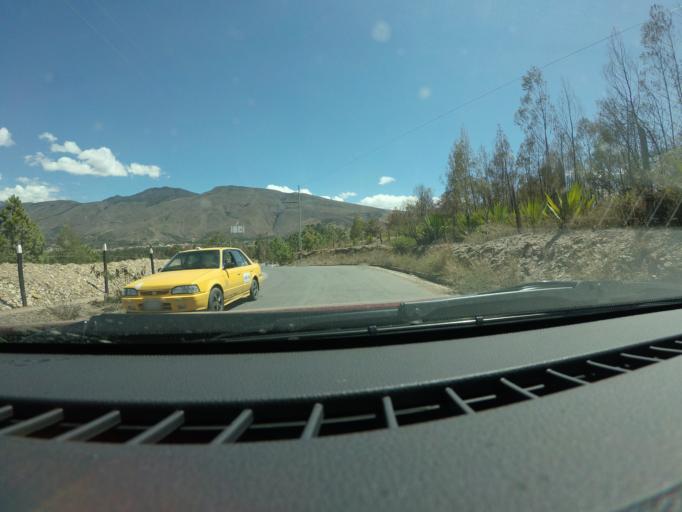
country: CO
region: Boyaca
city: Villa de Leiva
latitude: 5.6286
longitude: -73.5417
